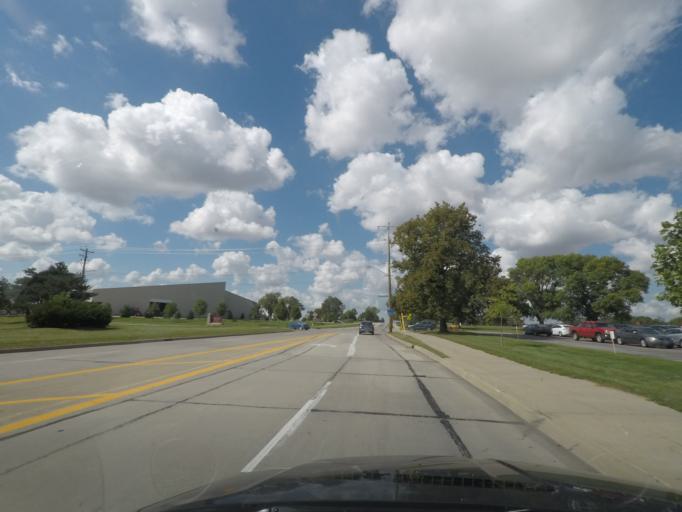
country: US
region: Iowa
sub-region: Story County
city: Ames
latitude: 42.0120
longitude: -93.6486
